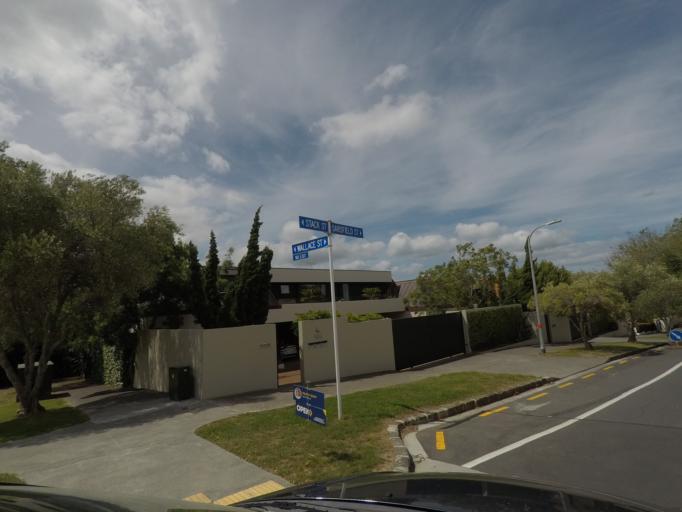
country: NZ
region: Auckland
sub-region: Auckland
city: Auckland
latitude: -36.8421
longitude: 174.7330
